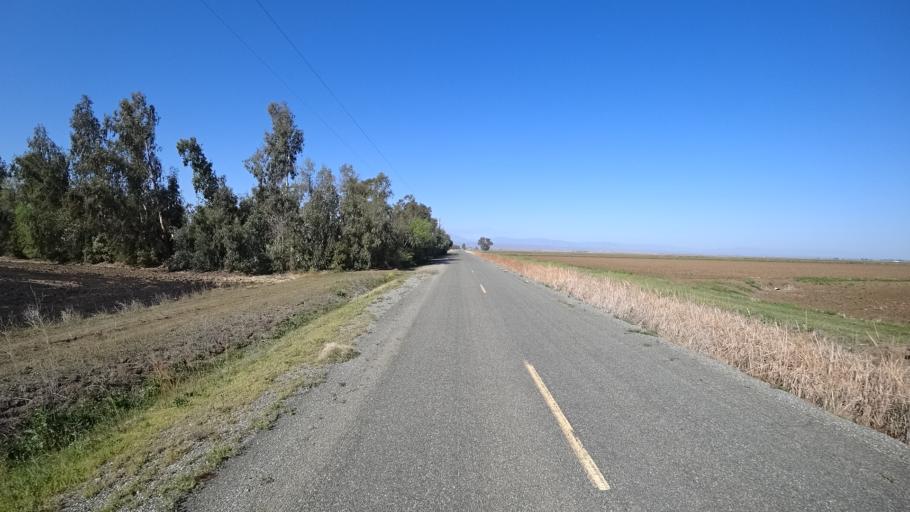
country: US
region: California
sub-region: Glenn County
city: Willows
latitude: 39.4510
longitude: -122.2002
